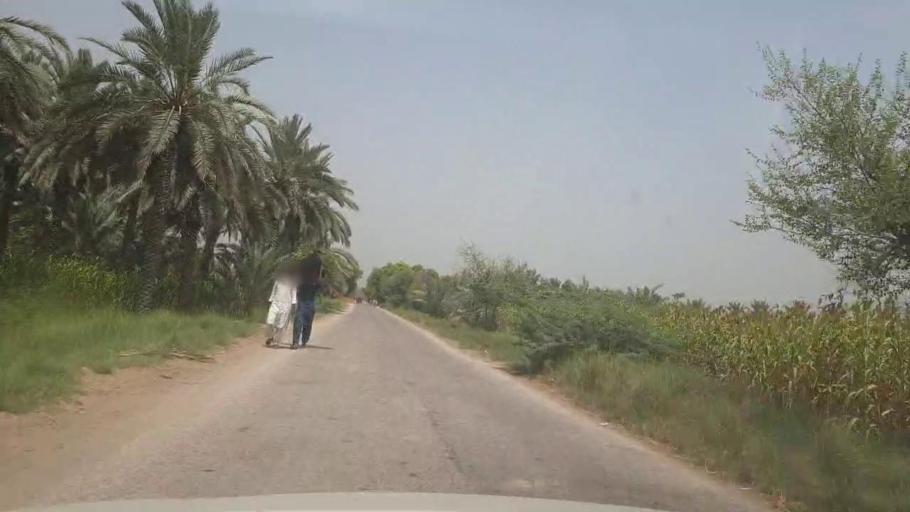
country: PK
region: Sindh
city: Kot Diji
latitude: 27.3620
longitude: 68.7004
